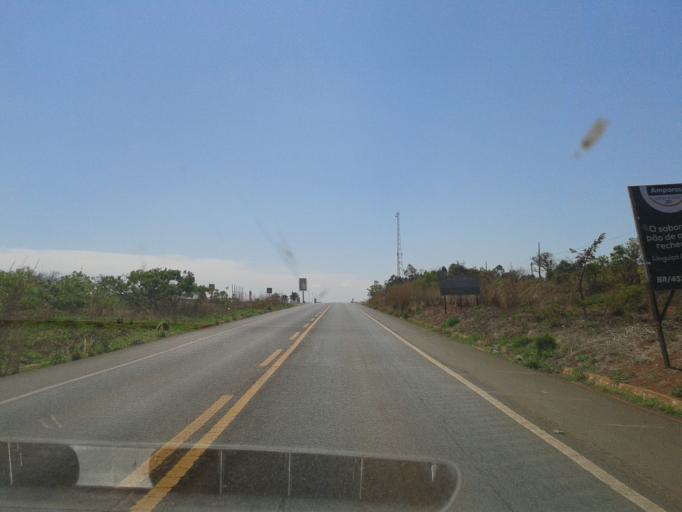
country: BR
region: Minas Gerais
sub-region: Sacramento
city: Sacramento
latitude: -19.3191
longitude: -47.5507
